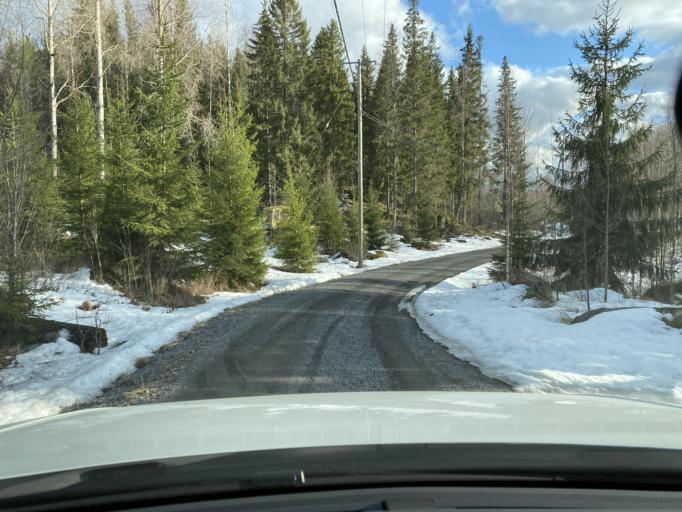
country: FI
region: Pirkanmaa
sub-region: Lounais-Pirkanmaa
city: Mouhijaervi
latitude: 61.4423
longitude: 22.9631
